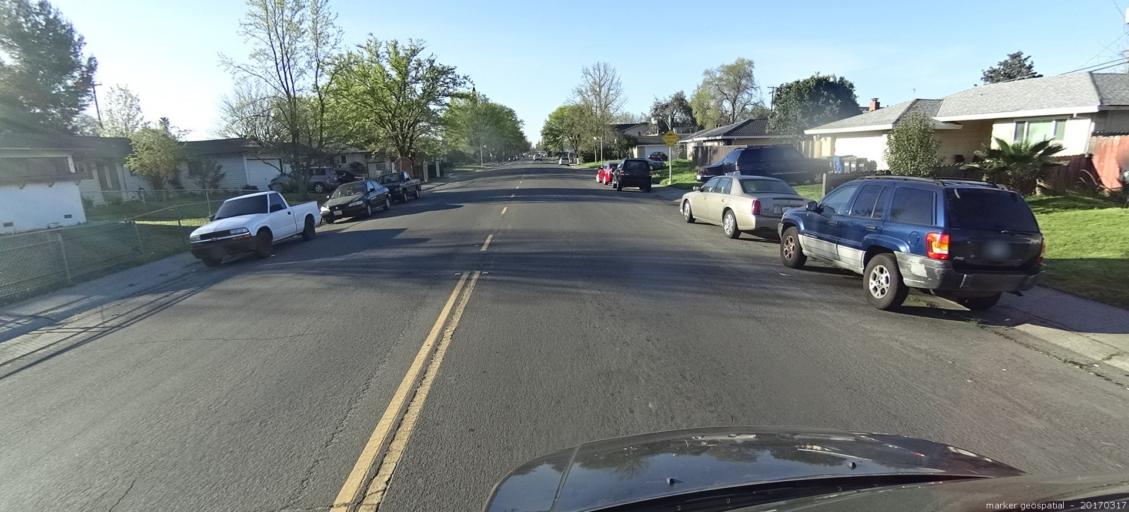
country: US
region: California
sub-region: Sacramento County
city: Parkway
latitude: 38.4933
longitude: -121.4920
